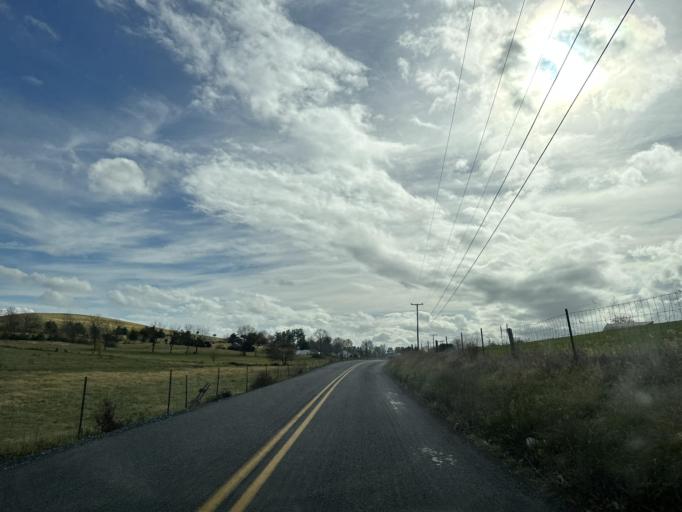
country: US
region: Virginia
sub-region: City of Harrisonburg
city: Harrisonburg
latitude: 38.4717
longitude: -78.8937
